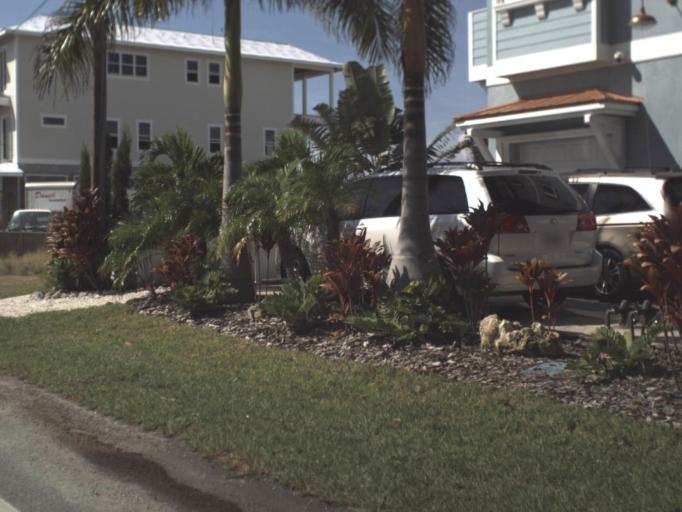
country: US
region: Florida
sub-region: Manatee County
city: Holmes Beach
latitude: 27.4834
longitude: -82.7052
